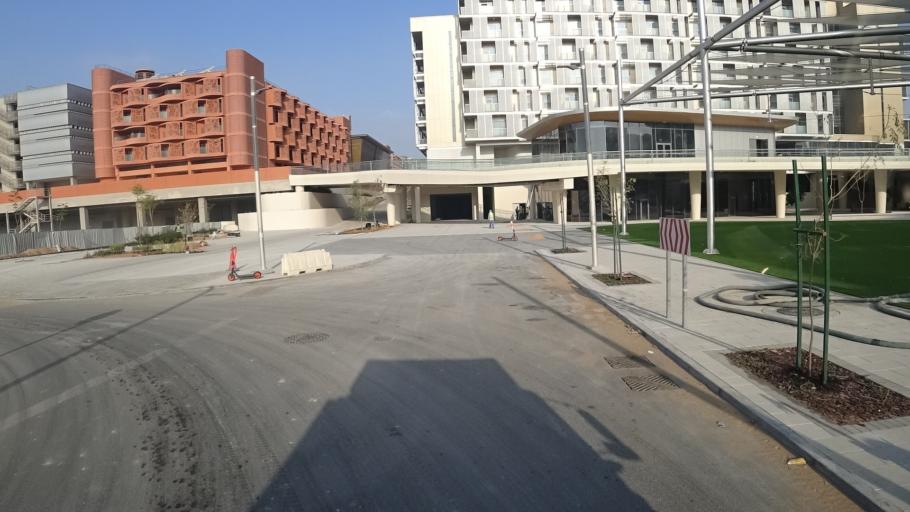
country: AE
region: Abu Dhabi
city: Abu Dhabi
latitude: 24.4328
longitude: 54.6204
